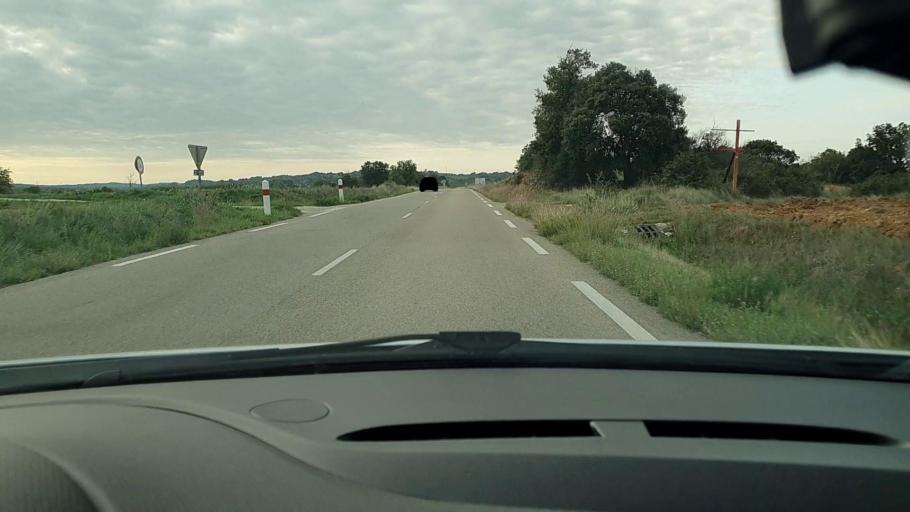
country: FR
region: Languedoc-Roussillon
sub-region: Departement du Gard
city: Mons
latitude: 44.0794
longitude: 4.2191
